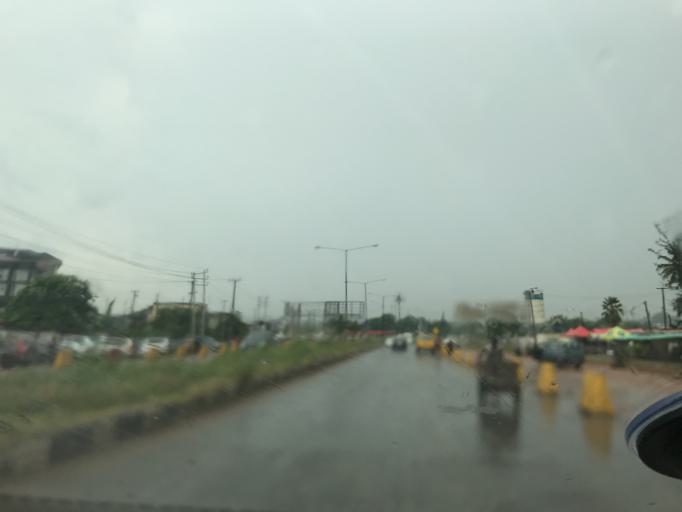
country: NG
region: Lagos
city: Oshodi
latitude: 6.5534
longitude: 3.3266
